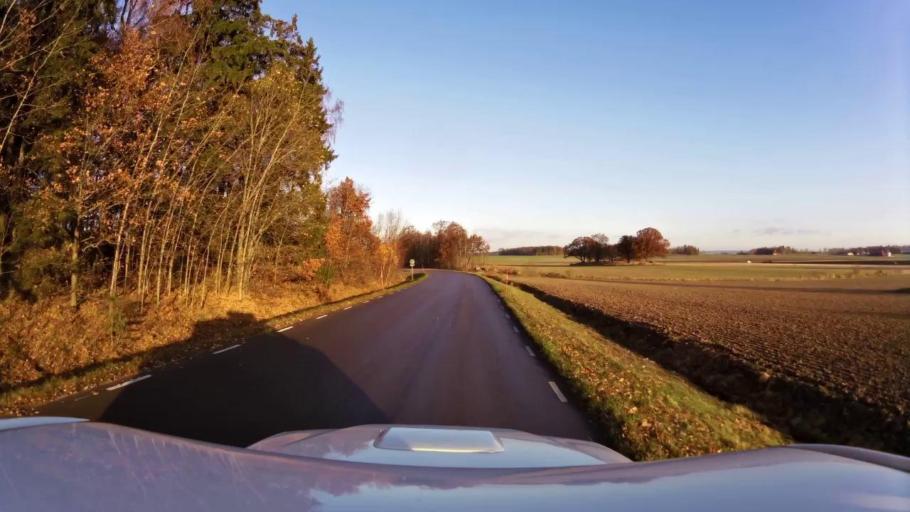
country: SE
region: OEstergoetland
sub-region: Linkopings Kommun
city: Ekangen
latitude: 58.4357
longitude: 15.6810
